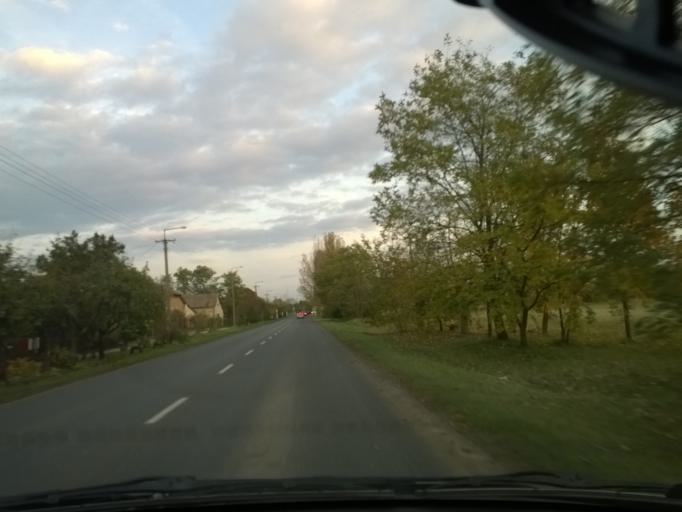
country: HU
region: Bacs-Kiskun
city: Palmonostora
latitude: 46.6856
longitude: 19.9524
